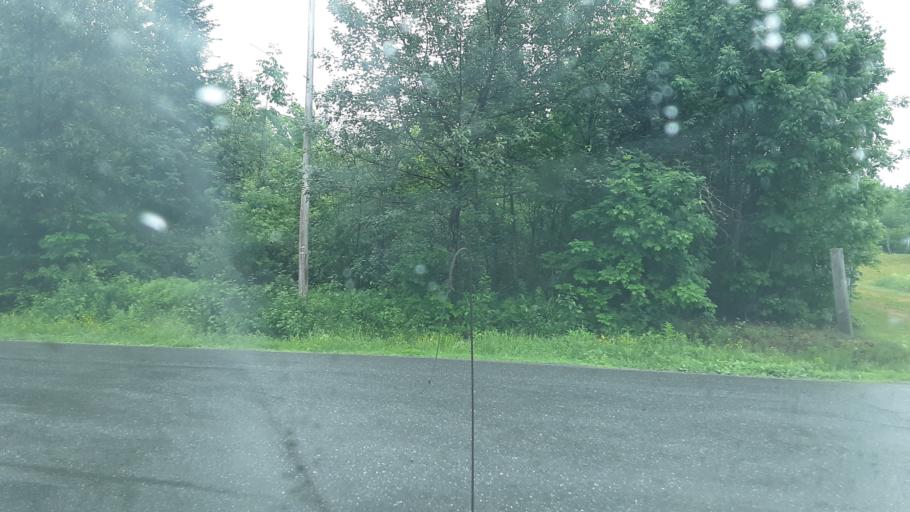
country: US
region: Maine
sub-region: Aroostook County
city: Presque Isle
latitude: 46.6813
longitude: -68.2162
